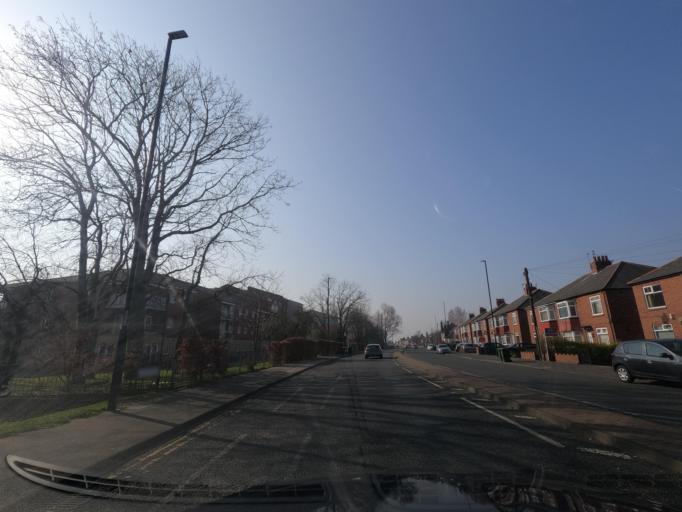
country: GB
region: England
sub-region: Newcastle upon Tyne
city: Gosforth
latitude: 55.0029
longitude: -1.5782
